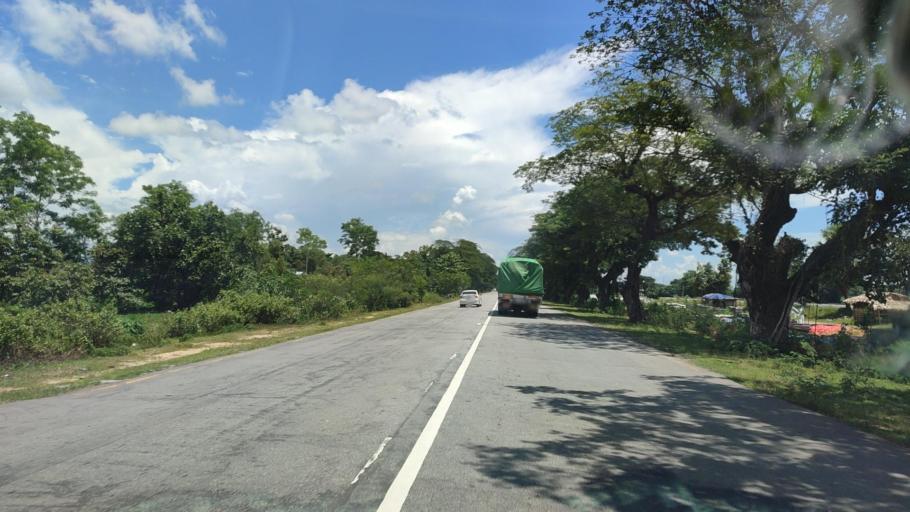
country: MM
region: Bago
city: Nyaunglebin
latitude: 18.1717
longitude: 96.6009
